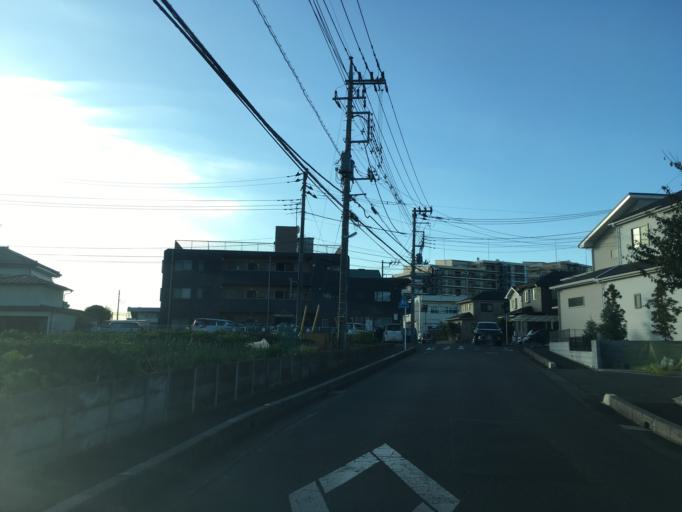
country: JP
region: Saitama
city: Tokorozawa
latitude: 35.7886
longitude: 139.4312
